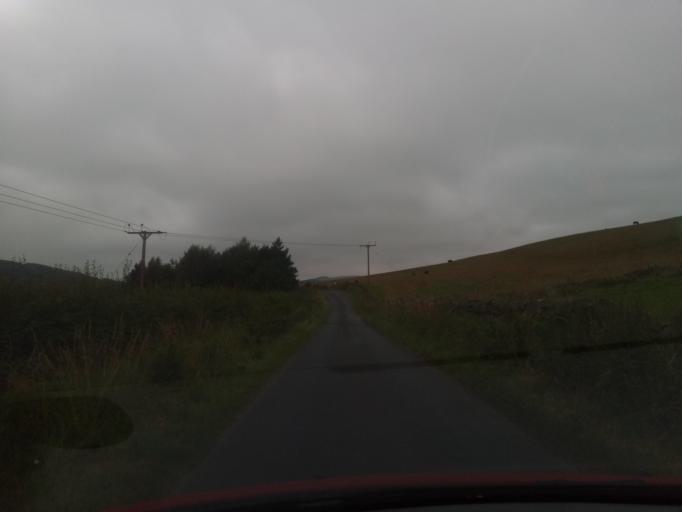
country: GB
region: Scotland
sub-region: The Scottish Borders
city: Galashiels
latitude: 55.6850
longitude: -2.8720
